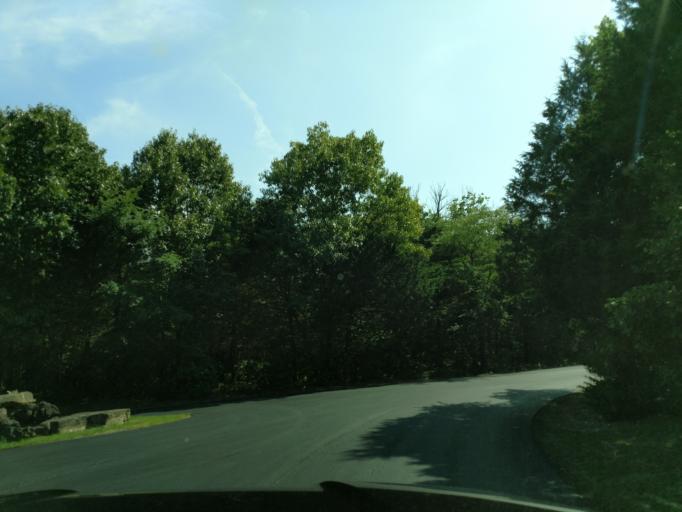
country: US
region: Missouri
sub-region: Barry County
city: Shell Knob
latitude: 36.6039
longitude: -93.5814
